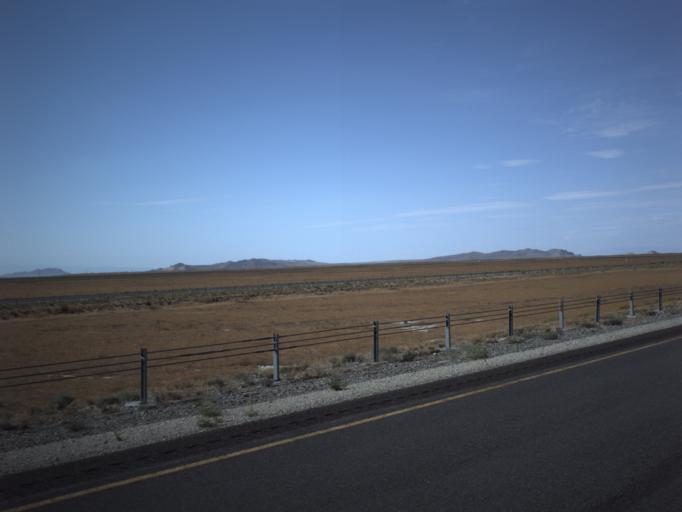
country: US
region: Utah
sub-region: Tooele County
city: Grantsville
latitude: 40.7260
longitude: -113.1457
